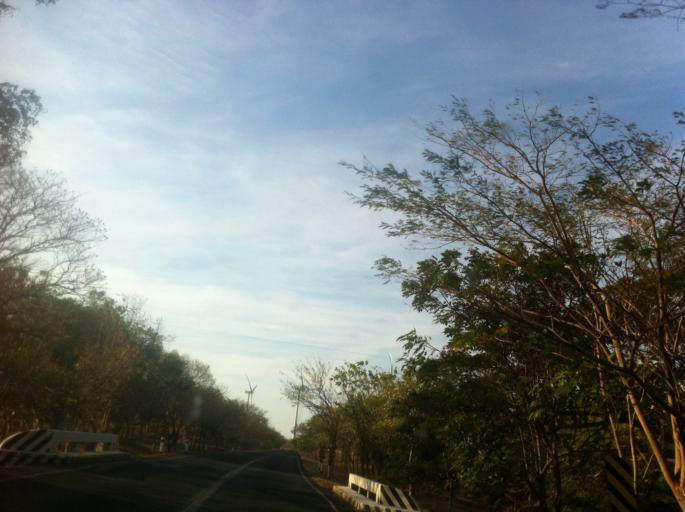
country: NI
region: Rivas
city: San Jorge
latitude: 11.3275
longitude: -85.7184
